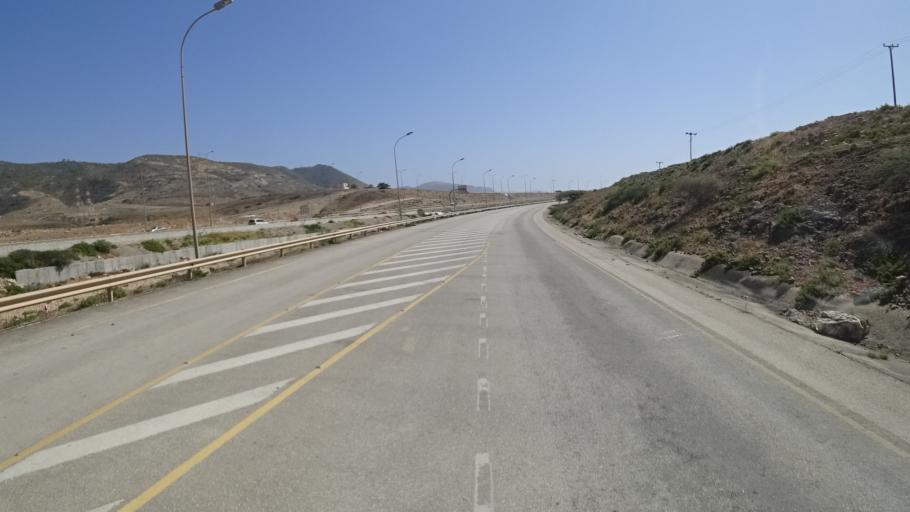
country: OM
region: Zufar
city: Salalah
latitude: 17.0591
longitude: 54.4345
